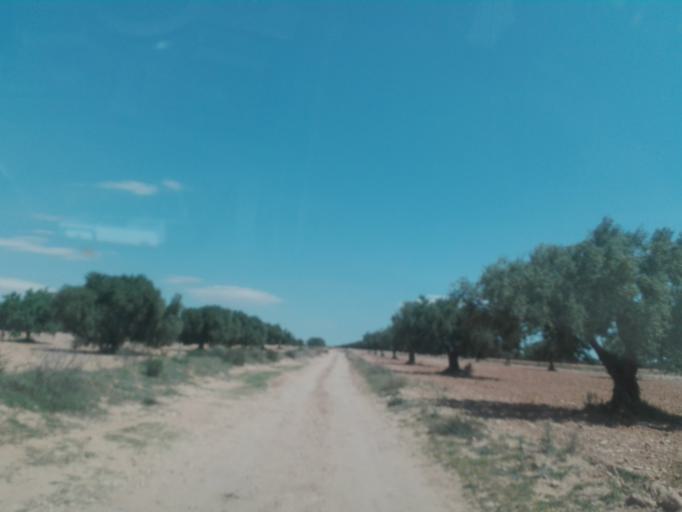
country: TN
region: Safaqis
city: Sfax
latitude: 34.6569
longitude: 10.5973
